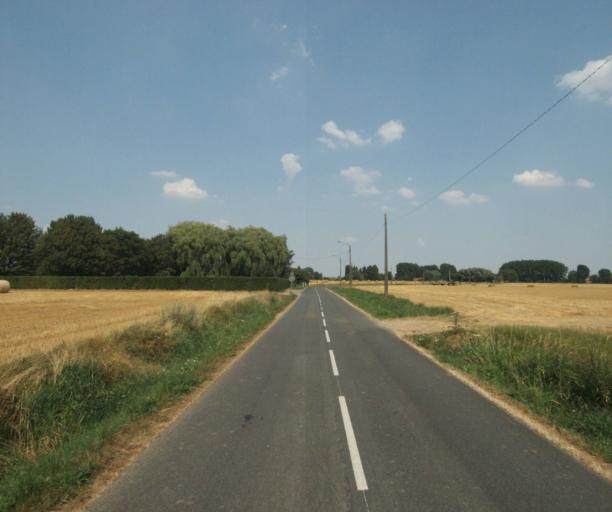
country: FR
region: Nord-Pas-de-Calais
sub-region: Departement du Nord
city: Linselles
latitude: 50.7257
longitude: 3.0442
